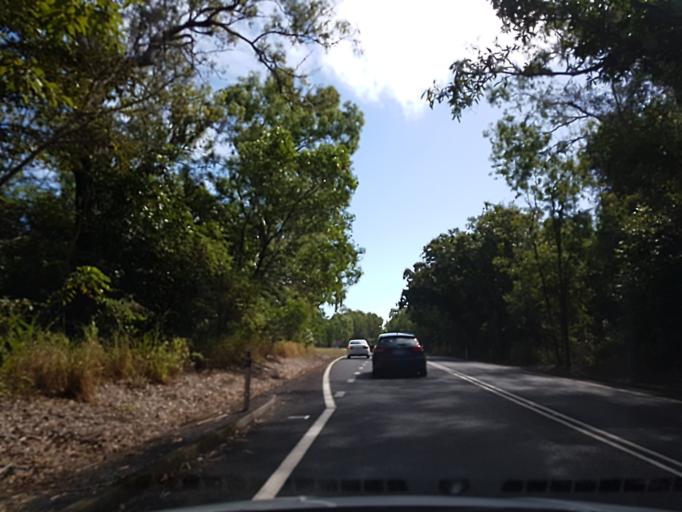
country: AU
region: Queensland
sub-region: Cairns
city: Palm Cove
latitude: -16.6634
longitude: 145.5665
